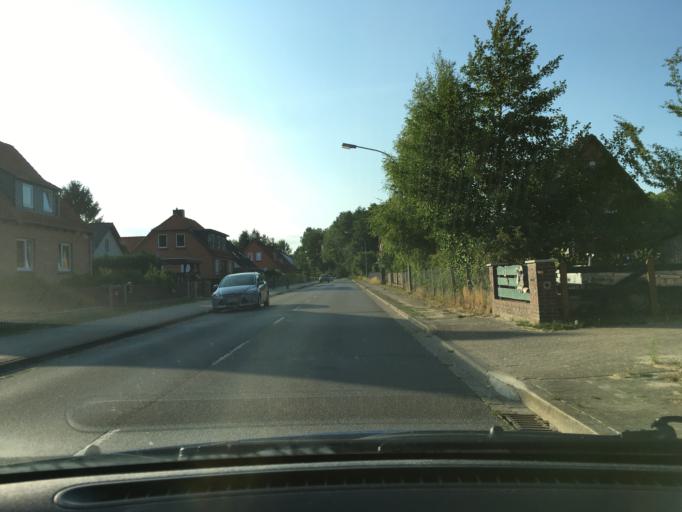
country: DE
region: Lower Saxony
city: Bienenbuttel
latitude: 53.1382
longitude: 10.5038
